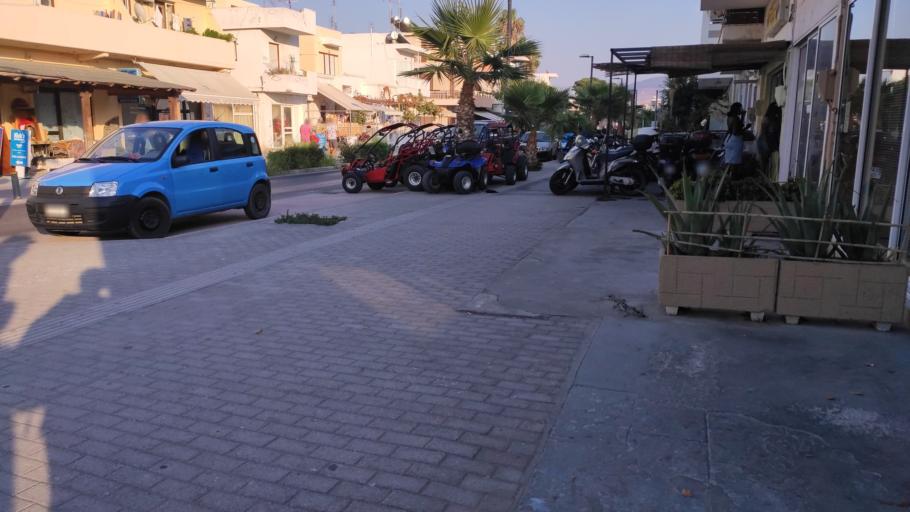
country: GR
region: South Aegean
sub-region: Nomos Dodekanisou
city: Kos
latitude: 36.9007
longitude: 27.2841
